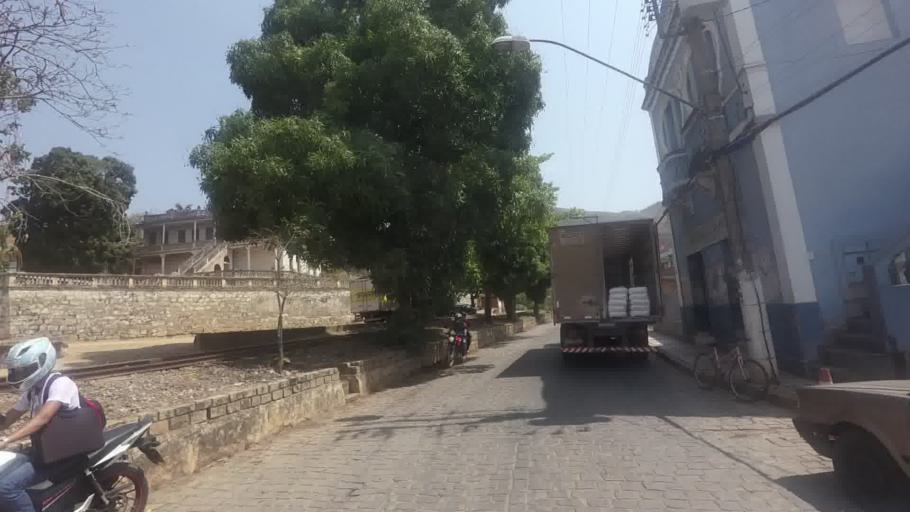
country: BR
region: Espirito Santo
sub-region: Mimoso Do Sul
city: Mimoso do Sul
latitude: -20.9547
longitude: -41.3509
